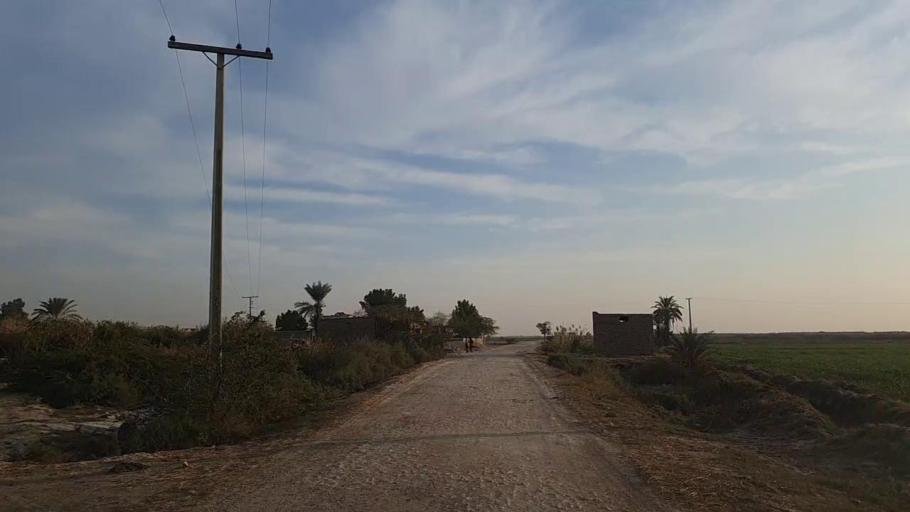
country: PK
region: Sindh
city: Bandhi
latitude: 26.5838
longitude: 68.3332
